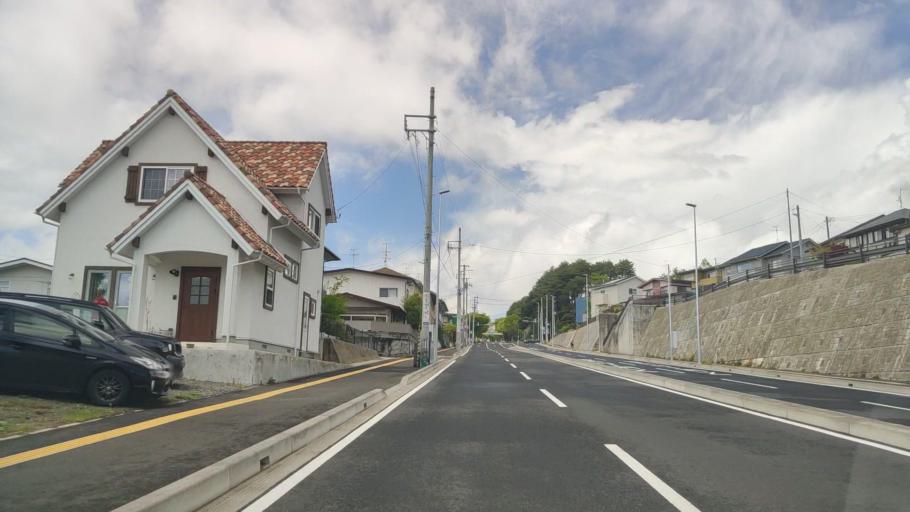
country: JP
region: Miyagi
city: Sendai
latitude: 38.2363
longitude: 140.8510
